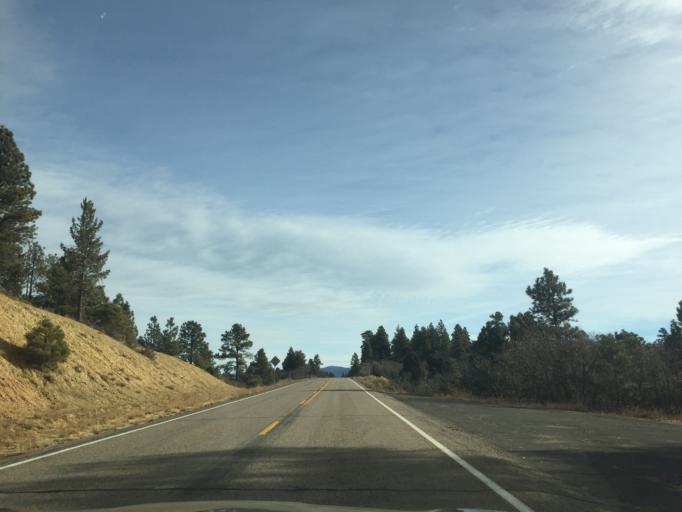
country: US
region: Utah
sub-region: Garfield County
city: Panguitch
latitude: 37.4952
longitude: -112.5528
